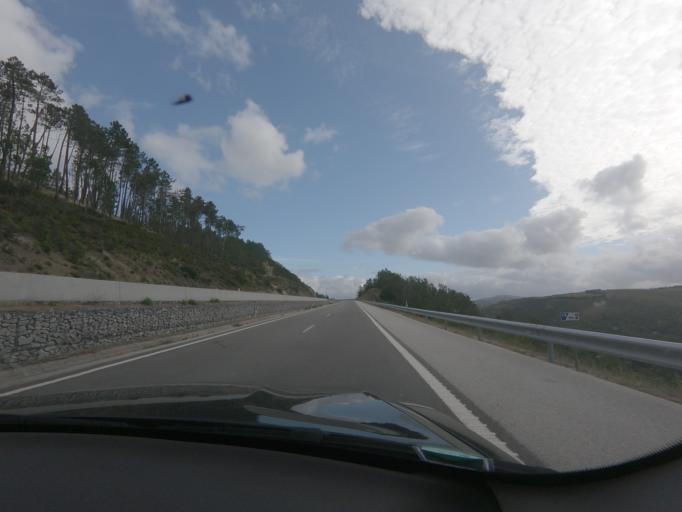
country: PT
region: Viseu
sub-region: Lamego
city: Lamego
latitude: 41.0471
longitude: -7.8597
